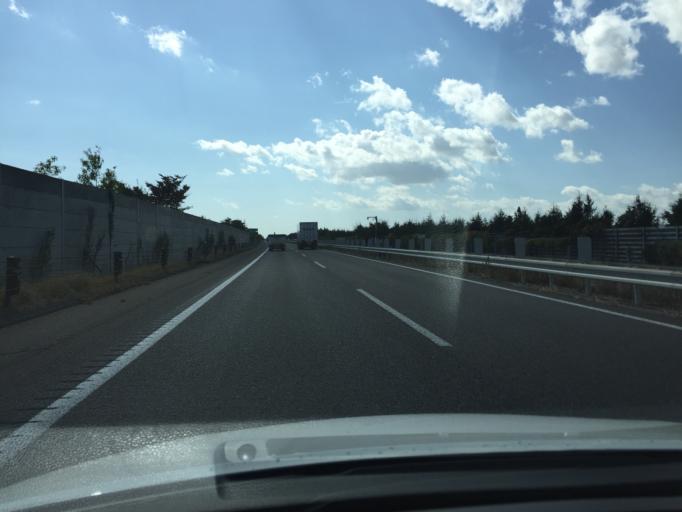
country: JP
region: Fukushima
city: Koriyama
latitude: 37.4514
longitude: 140.3537
